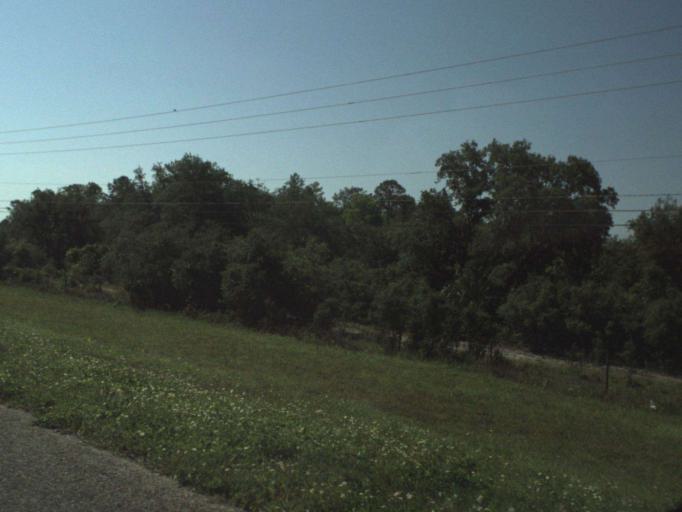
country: US
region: Florida
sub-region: Orange County
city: Christmas
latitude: 28.4697
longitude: -81.0065
